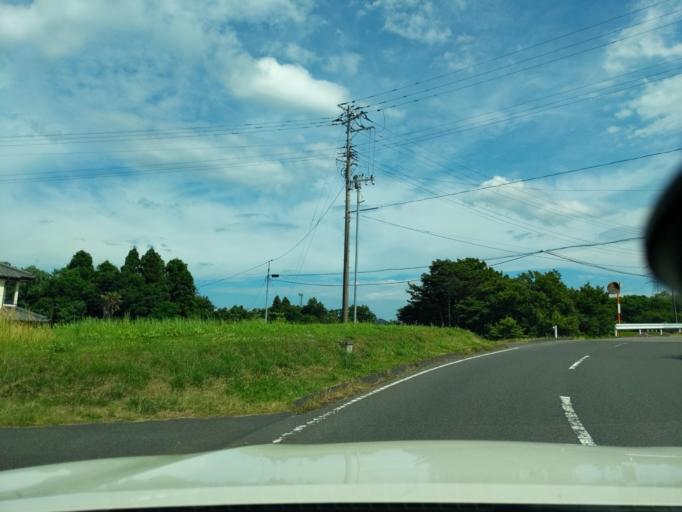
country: JP
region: Fukushima
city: Koriyama
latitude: 37.4377
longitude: 140.3950
